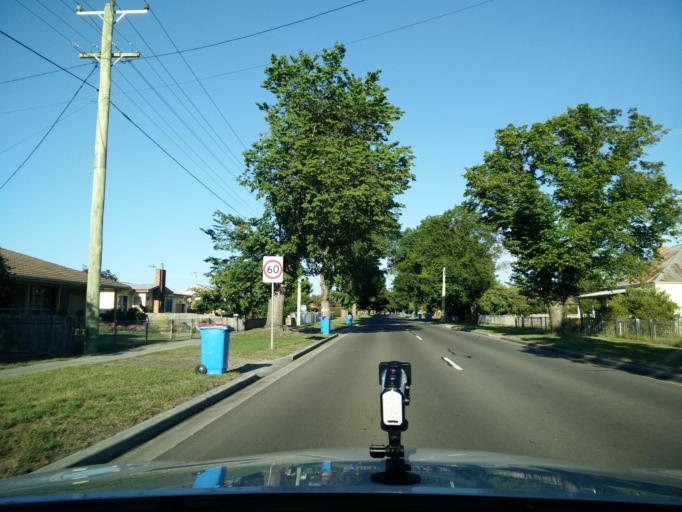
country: AU
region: Tasmania
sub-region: Break O'Day
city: St Helens
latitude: -41.3178
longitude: 148.2469
